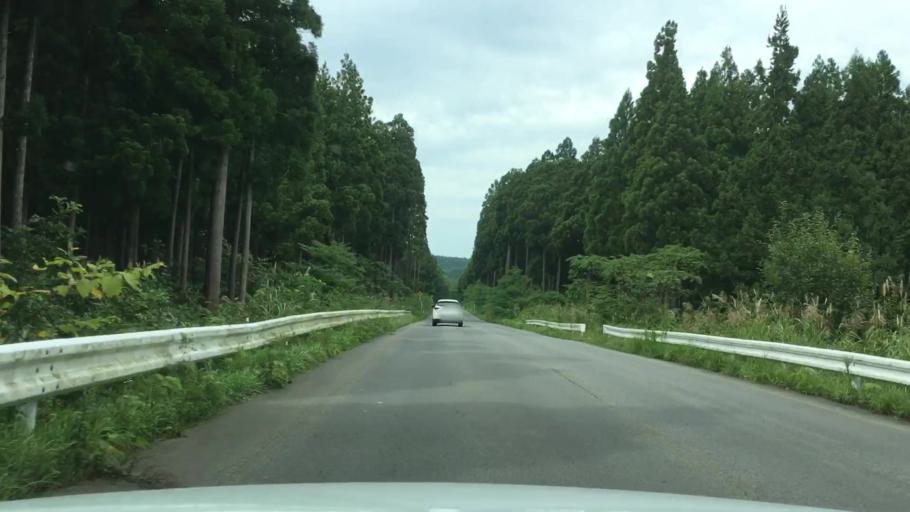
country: JP
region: Aomori
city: Shimokizukuri
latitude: 40.7108
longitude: 140.2719
